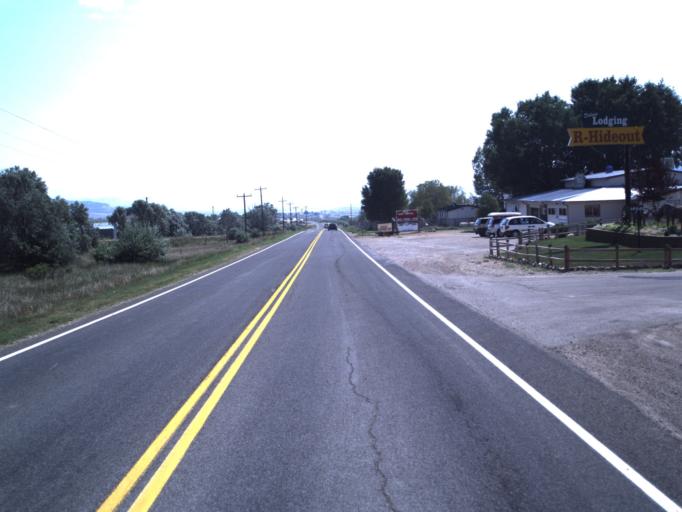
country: US
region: Utah
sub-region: Daggett County
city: Manila
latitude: 40.9883
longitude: -109.7180
